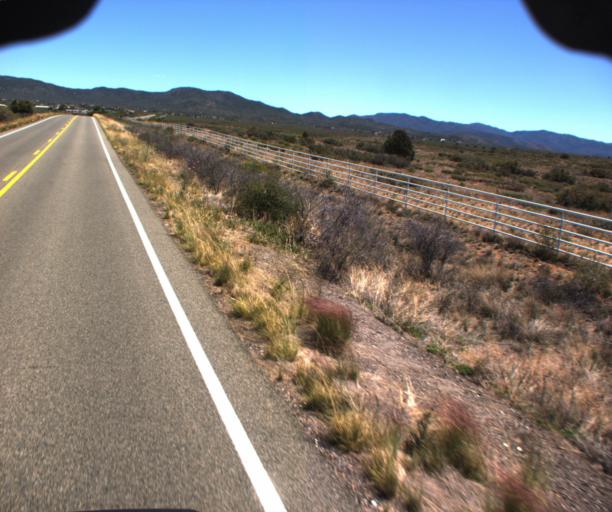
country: US
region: Arizona
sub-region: Yavapai County
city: Prescott
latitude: 34.4080
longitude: -112.6153
